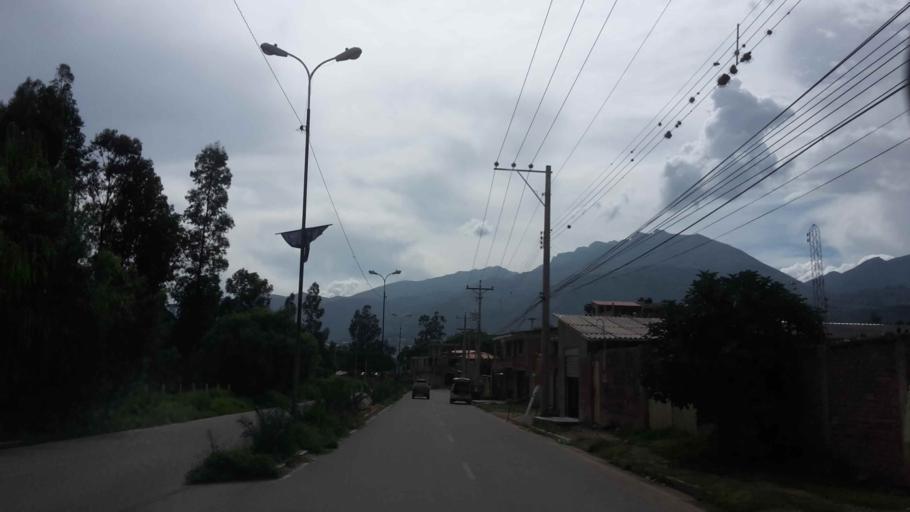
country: BO
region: Cochabamba
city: Cochabamba
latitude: -17.3289
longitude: -66.2449
